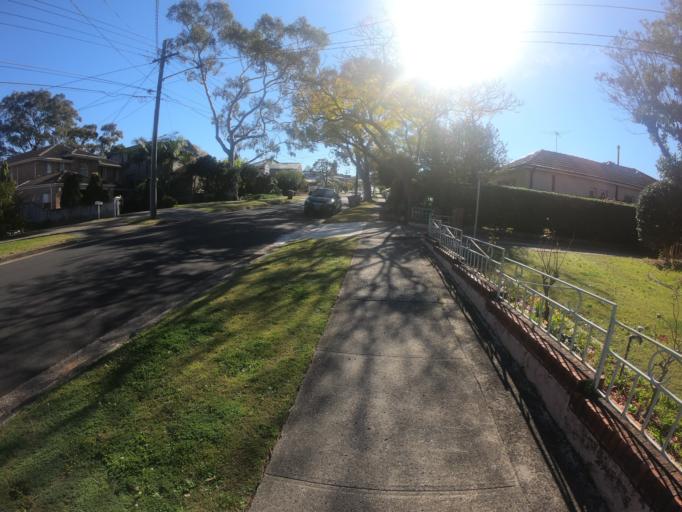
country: AU
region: New South Wales
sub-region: Ryde
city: East Ryde
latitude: -33.8230
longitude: 151.1138
